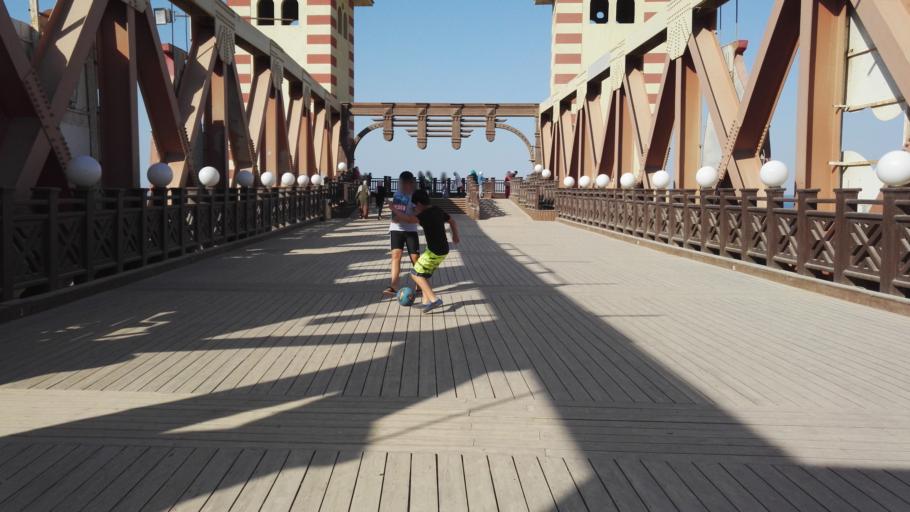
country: EG
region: As Suways
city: Ain Sukhna
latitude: 29.4437
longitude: 32.4831
